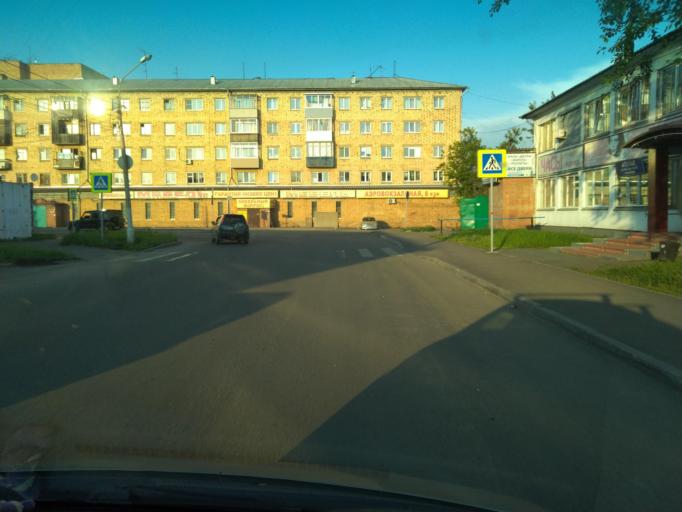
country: RU
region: Krasnoyarskiy
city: Krasnoyarsk
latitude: 56.0287
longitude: 92.8990
